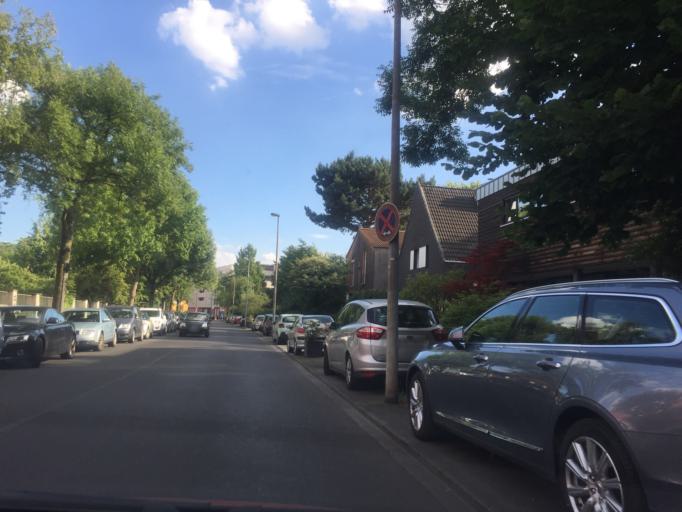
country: DE
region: North Rhine-Westphalia
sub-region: Regierungsbezirk Koln
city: Poll
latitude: 50.8940
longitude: 6.9897
